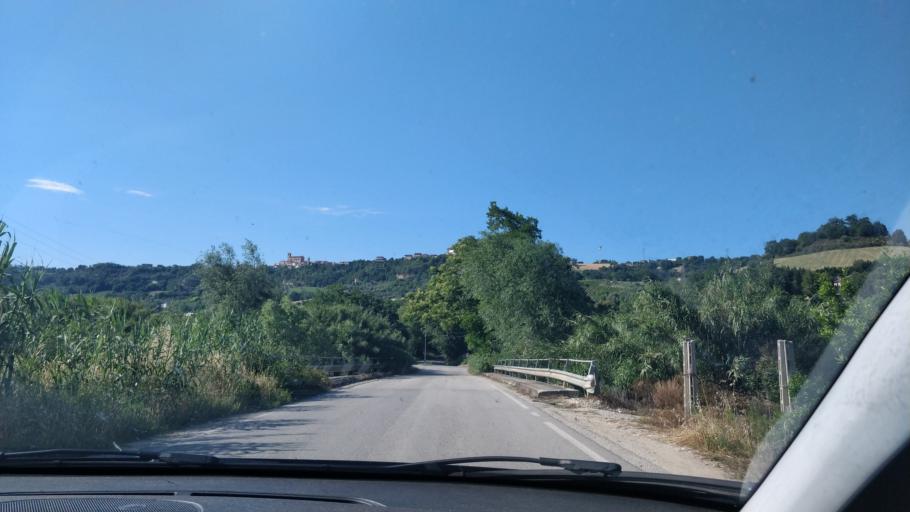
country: IT
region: The Marches
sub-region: Provincia di Ascoli Piceno
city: Massignano
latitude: 43.0359
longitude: 13.8004
